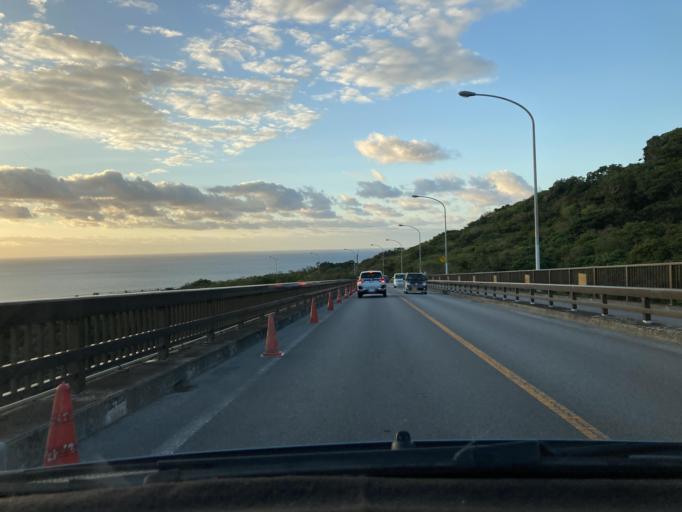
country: JP
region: Okinawa
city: Ginowan
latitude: 26.1664
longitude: 127.8161
